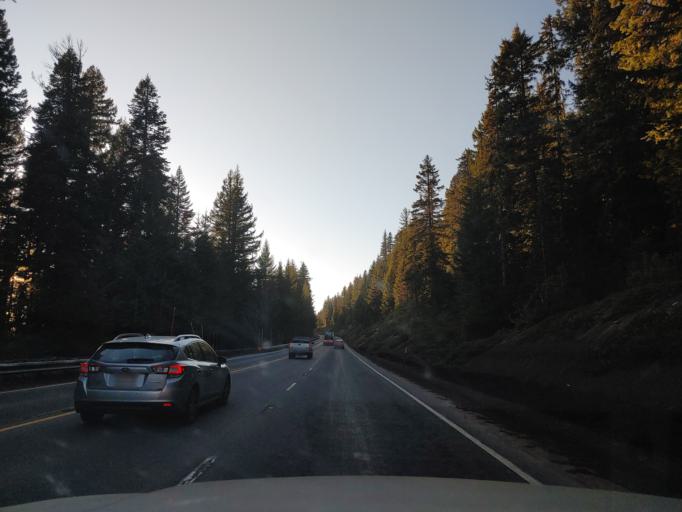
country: US
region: Oregon
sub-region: Lane County
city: Oakridge
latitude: 43.5890
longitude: -122.0174
